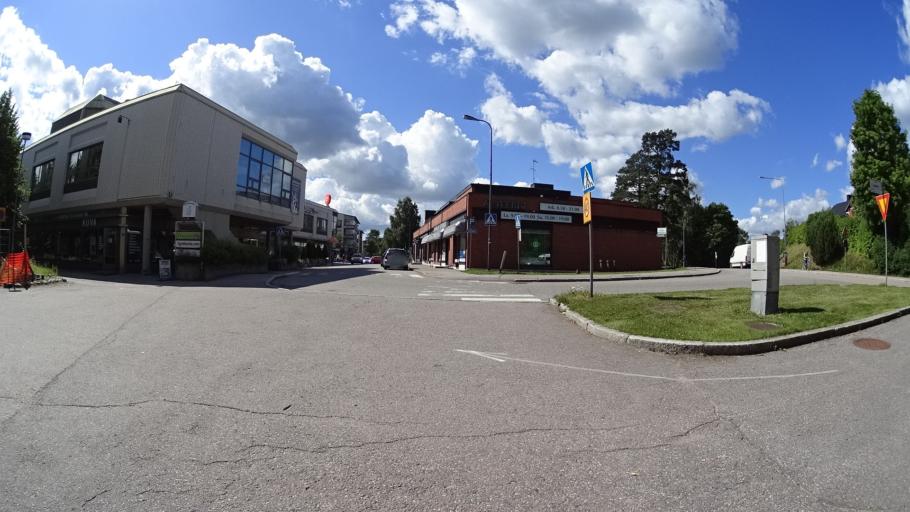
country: FI
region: Uusimaa
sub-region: Helsinki
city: Tuusula
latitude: 60.4013
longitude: 25.0232
